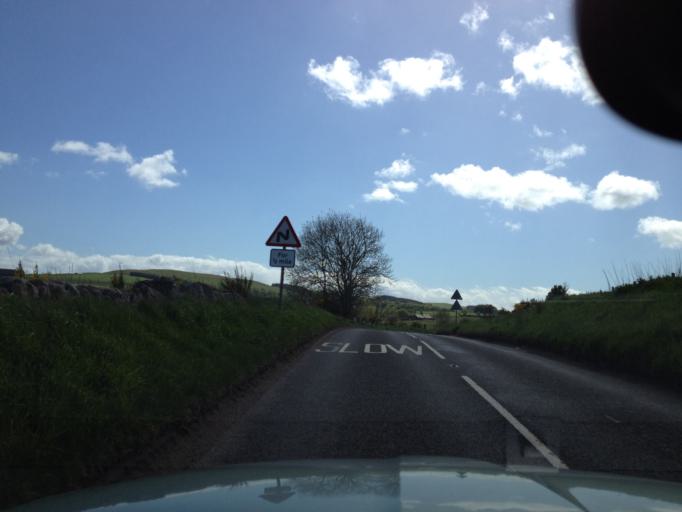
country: GB
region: Scotland
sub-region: Angus
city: Letham
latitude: 56.6903
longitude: -2.7835
